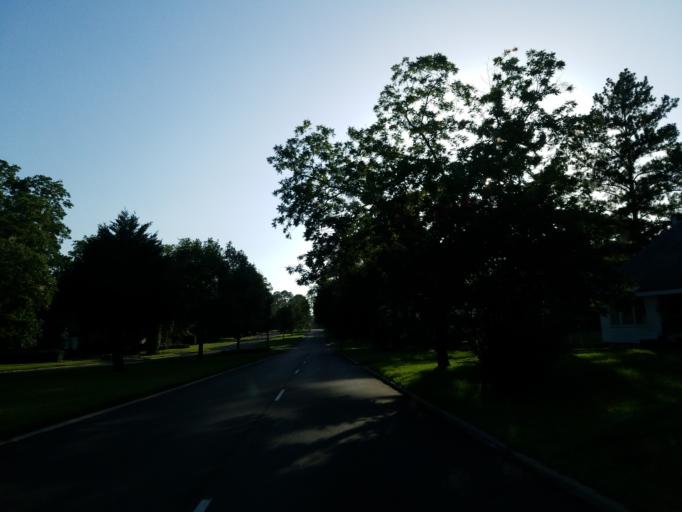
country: US
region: Georgia
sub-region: Ben Hill County
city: Fitzgerald
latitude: 31.7149
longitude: -83.2614
